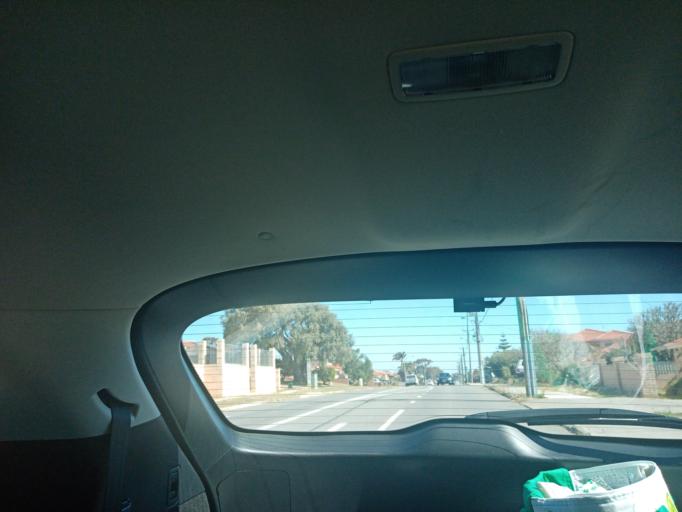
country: AU
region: Western Australia
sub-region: City of Cockburn
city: Spearwood
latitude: -32.1112
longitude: 115.7826
